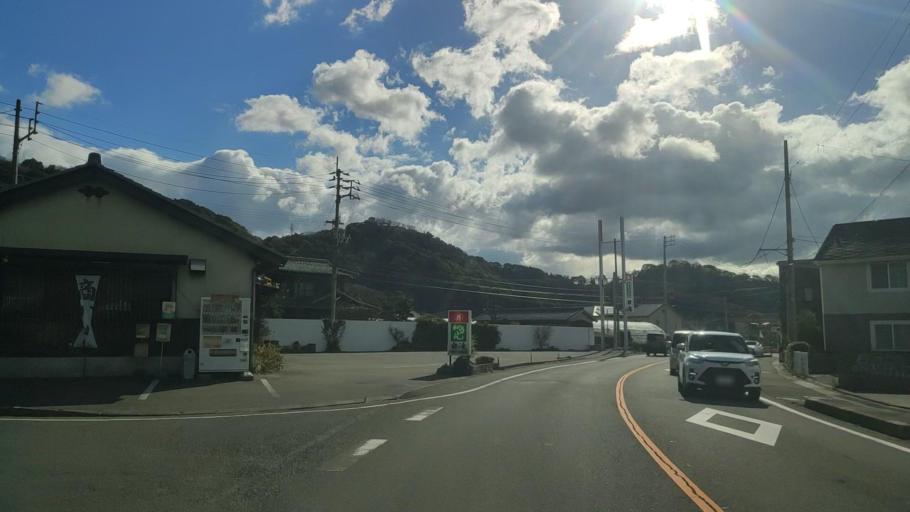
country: JP
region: Ehime
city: Masaki-cho
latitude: 33.8409
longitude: 132.7089
